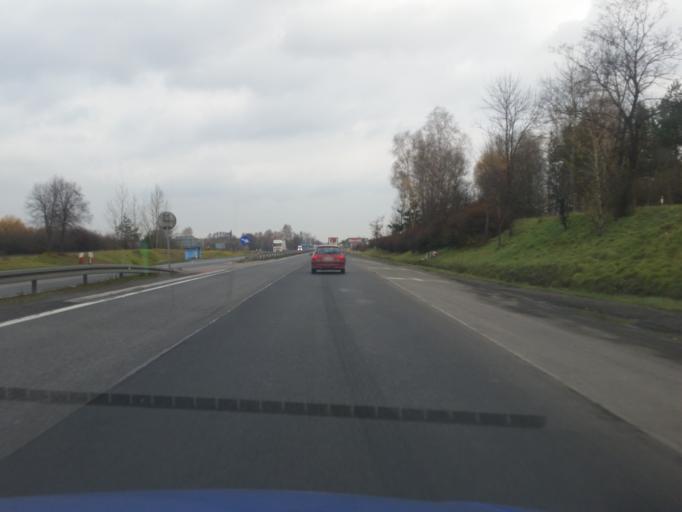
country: PL
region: Silesian Voivodeship
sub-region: Powiat czestochowski
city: Kamienica Polska
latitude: 50.6787
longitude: 19.1273
